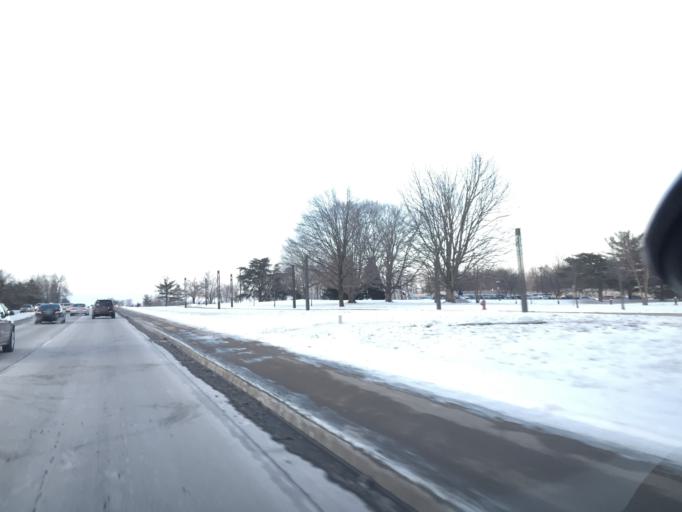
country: US
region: Indiana
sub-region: Monroe County
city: Bloomington
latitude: 39.1724
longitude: -86.5026
